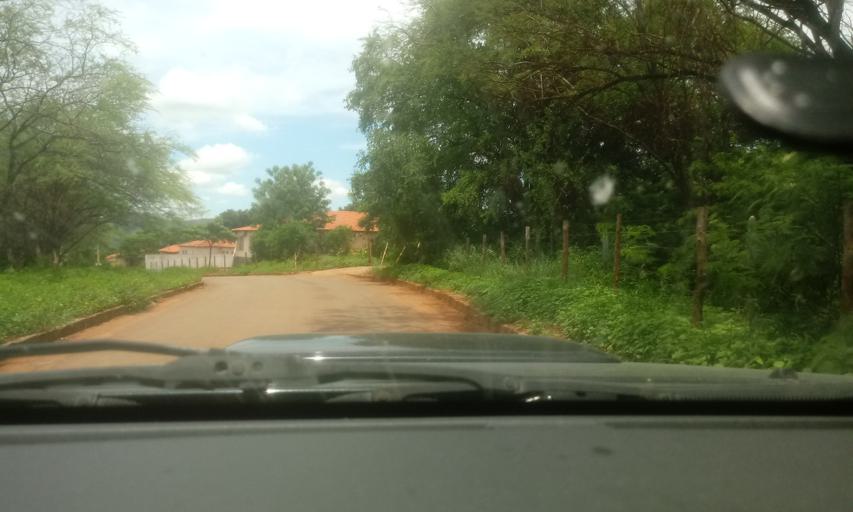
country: BR
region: Bahia
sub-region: Riacho De Santana
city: Riacho de Santana
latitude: -13.6007
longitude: -42.9453
